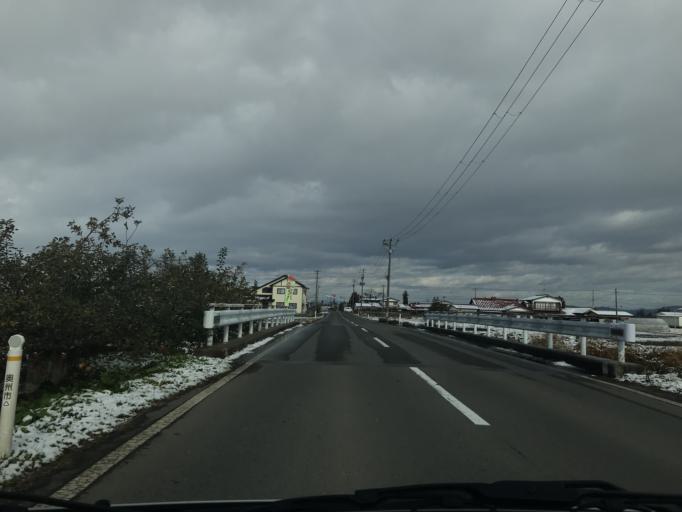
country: JP
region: Iwate
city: Mizusawa
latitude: 39.1608
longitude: 141.1116
